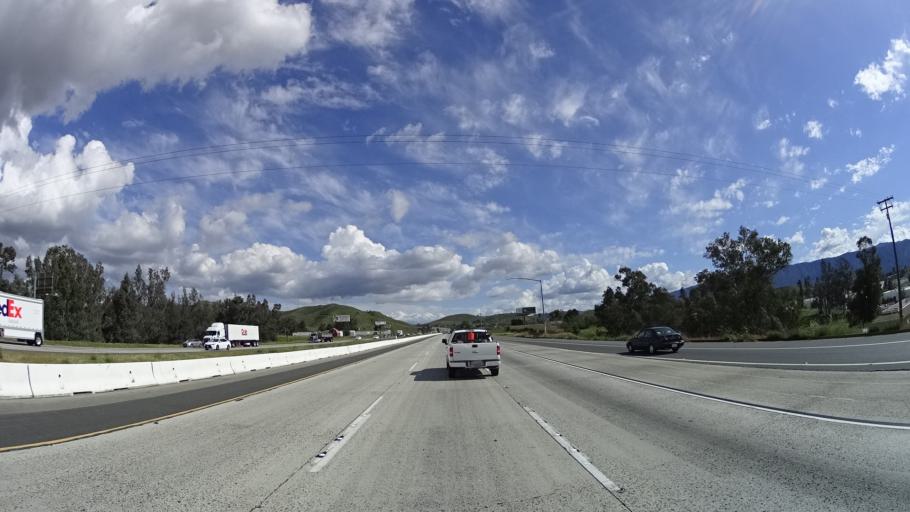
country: US
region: California
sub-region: Riverside County
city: Lake Elsinore
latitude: 33.6893
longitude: -117.3353
